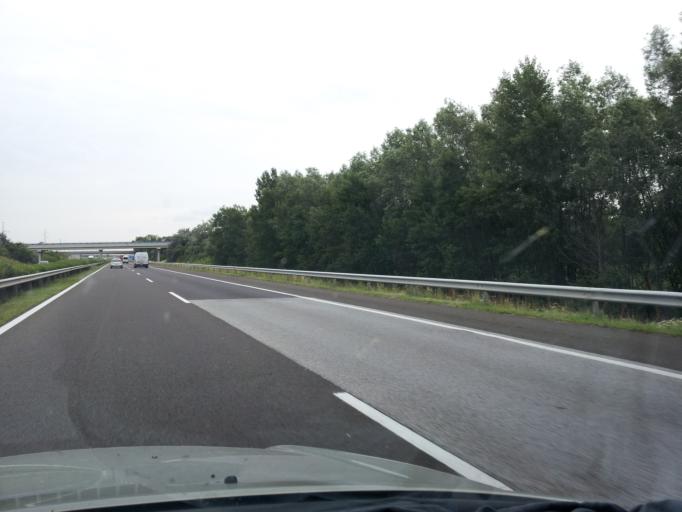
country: HU
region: Heves
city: Gyongyoshalasz
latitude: 47.7305
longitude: 19.9293
